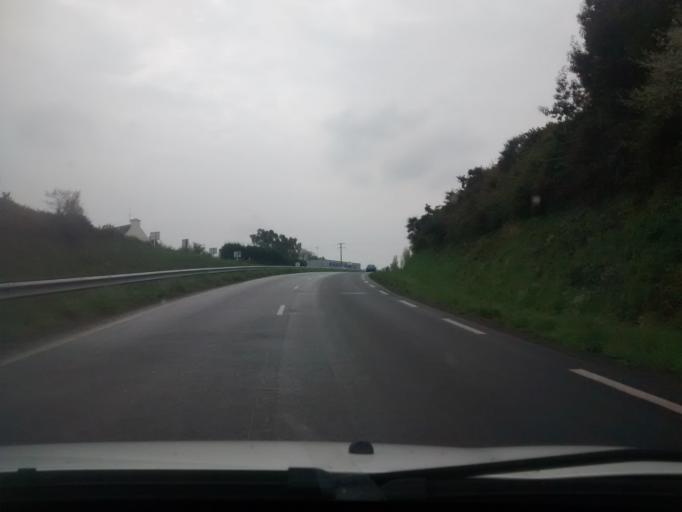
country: FR
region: Brittany
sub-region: Departement des Cotes-d'Armor
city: Saint-Quay-Perros
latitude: 48.7914
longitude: -3.4421
